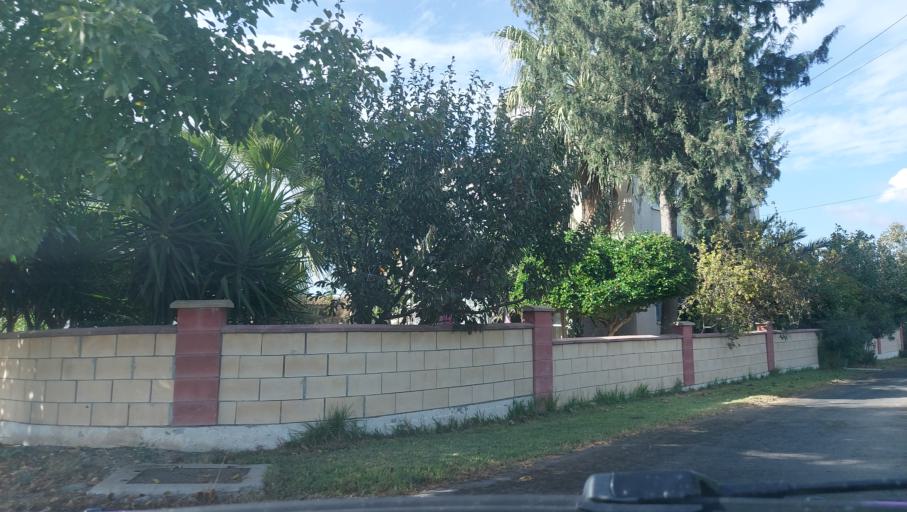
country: CY
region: Lefkosia
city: Pano Deftera
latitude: 35.0844
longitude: 33.2644
